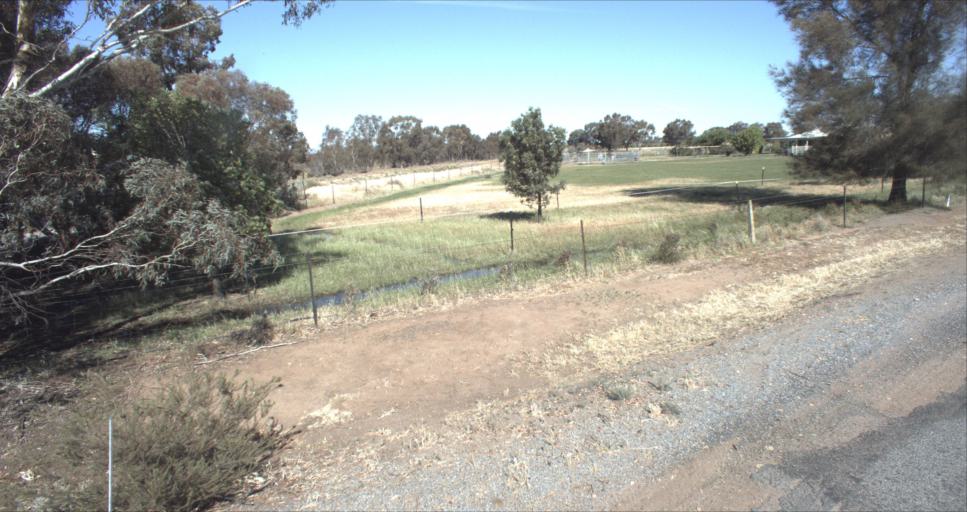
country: AU
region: New South Wales
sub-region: Leeton
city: Leeton
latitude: -34.5357
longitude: 146.4200
